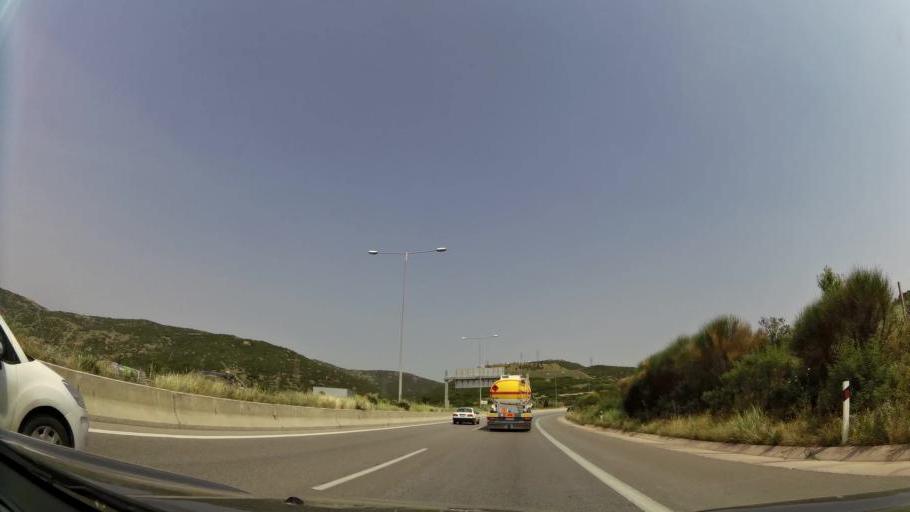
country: GR
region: Central Macedonia
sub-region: Nomos Thessalonikis
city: Efkarpia
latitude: 40.6944
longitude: 22.9616
